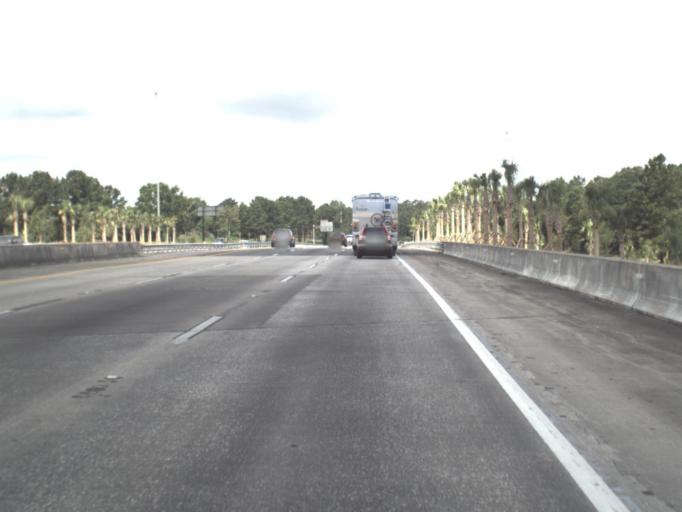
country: US
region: Florida
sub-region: Alachua County
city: High Springs
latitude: 29.9999
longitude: -82.5971
